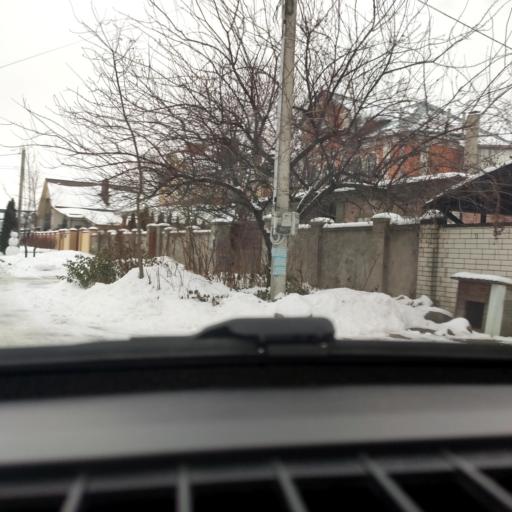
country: RU
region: Voronezj
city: Somovo
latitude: 51.6871
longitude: 39.3097
